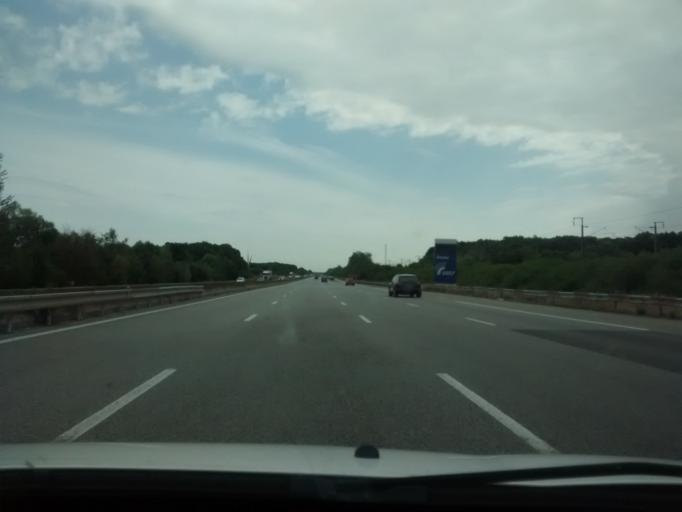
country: FR
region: Ile-de-France
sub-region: Departement de l'Essonne
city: Angervilliers
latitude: 48.6021
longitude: 2.0688
